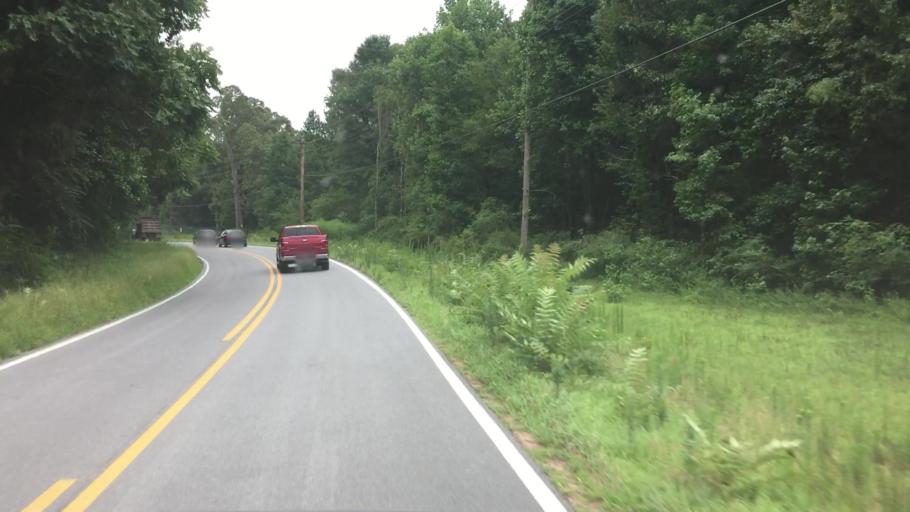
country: US
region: Georgia
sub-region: Barrow County
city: Winder
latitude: 34.0330
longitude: -83.7211
